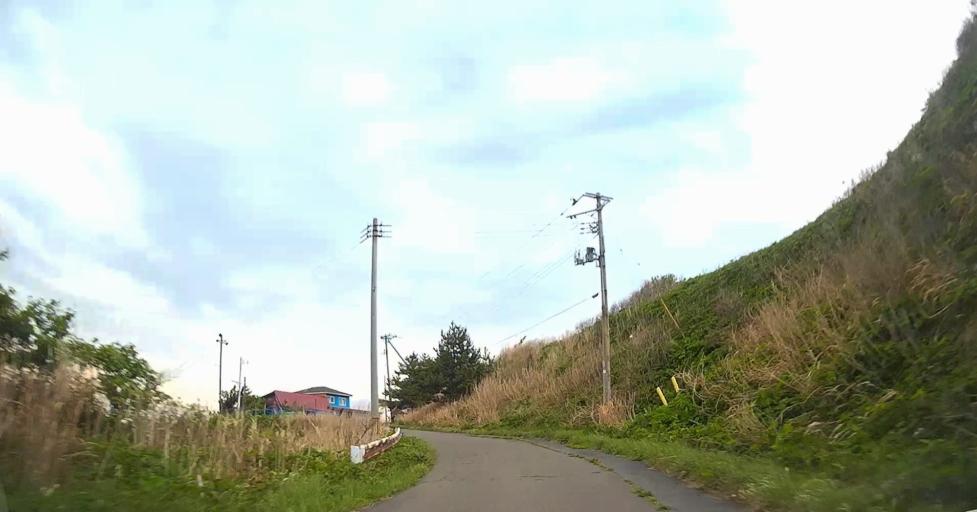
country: JP
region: Aomori
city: Shimokizukuri
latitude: 41.2427
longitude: 140.3421
